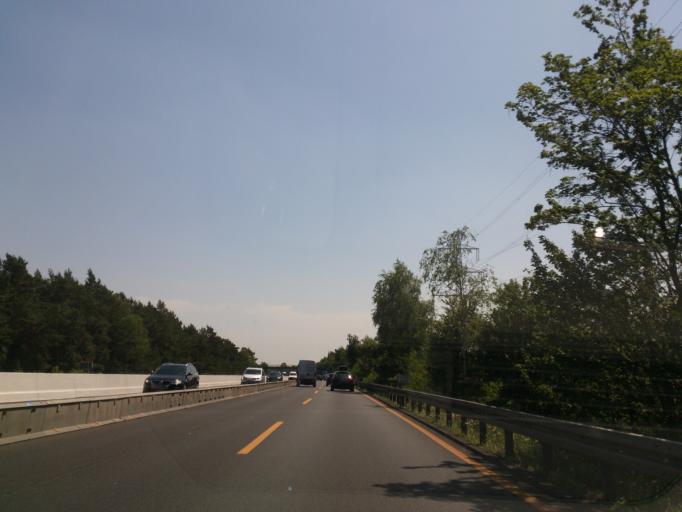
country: DE
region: North Rhine-Westphalia
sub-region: Regierungsbezirk Detmold
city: Hovelhof
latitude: 51.8458
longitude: 8.6757
